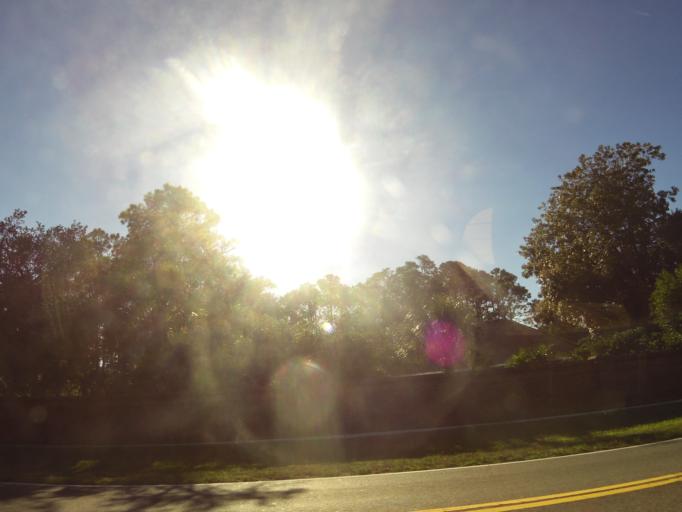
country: US
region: Florida
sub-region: Duval County
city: Neptune Beach
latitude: 30.3104
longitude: -81.4466
